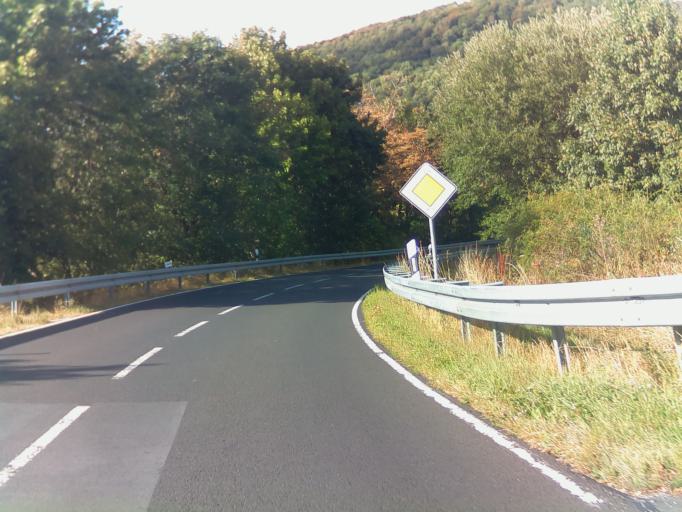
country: DE
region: Thuringia
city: Birx
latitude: 50.5195
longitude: 10.0353
